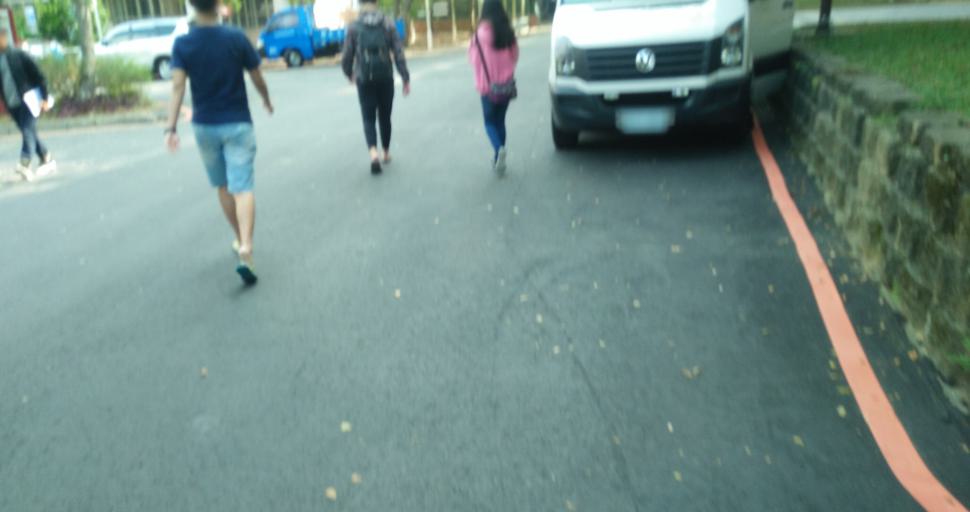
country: TW
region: Taiwan
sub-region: Hsinchu
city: Hsinchu
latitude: 24.7589
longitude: 120.9549
